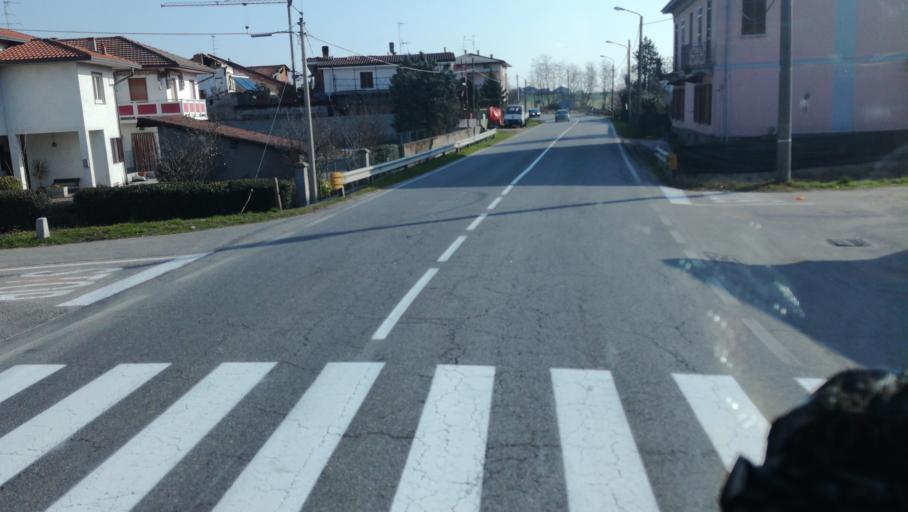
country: IT
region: Piedmont
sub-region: Provincia di Novara
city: Momo
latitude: 45.5861
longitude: 8.5832
